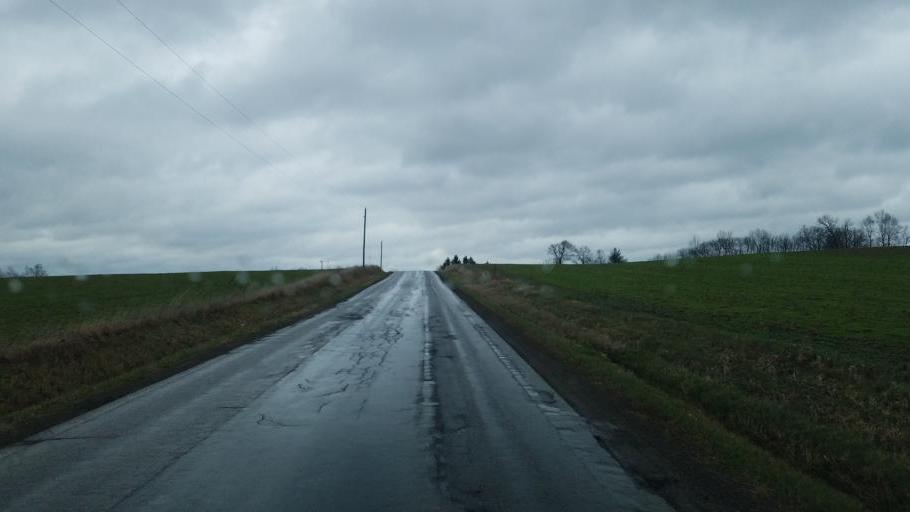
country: US
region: Ohio
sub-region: Wayne County
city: Apple Creek
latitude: 40.6874
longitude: -81.8183
